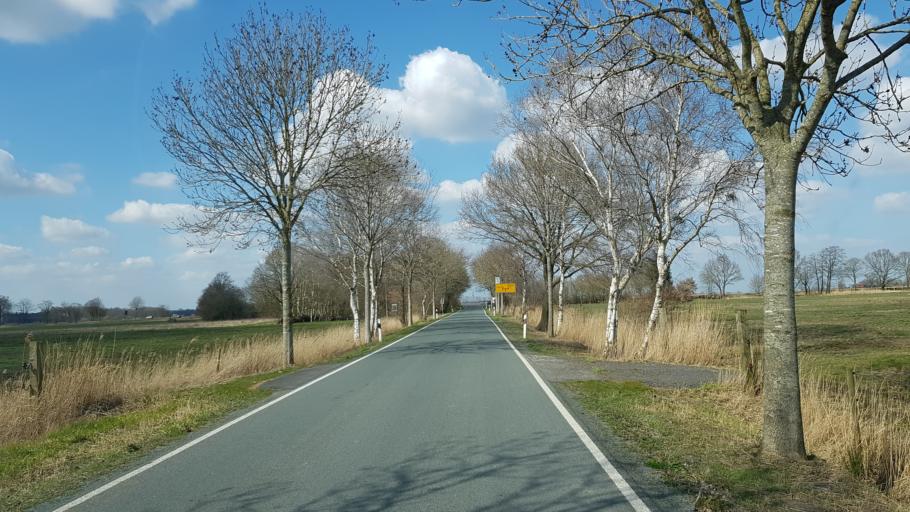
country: DE
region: Lower Saxony
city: Rastede
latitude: 53.3371
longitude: 8.2219
